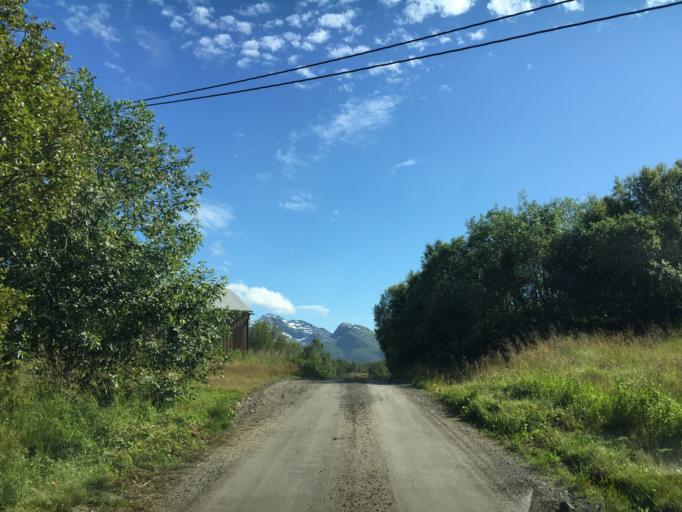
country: NO
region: Nordland
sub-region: Vagan
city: Kabelvag
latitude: 68.3517
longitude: 14.4520
